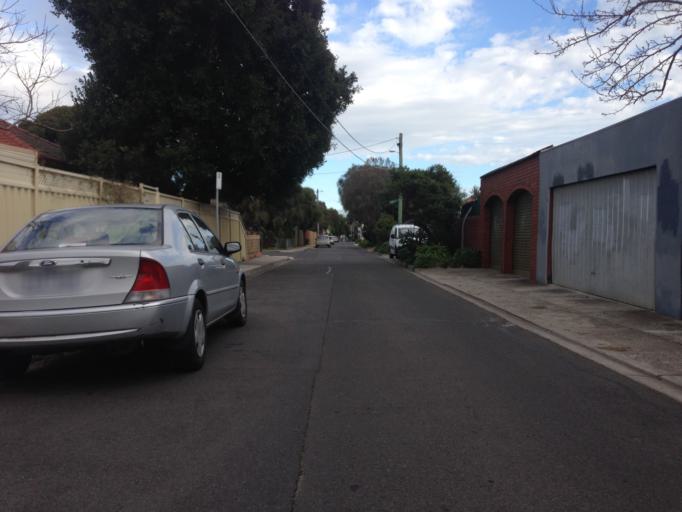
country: AU
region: Victoria
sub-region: Darebin
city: Fairfield
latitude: -37.7758
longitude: 145.0204
